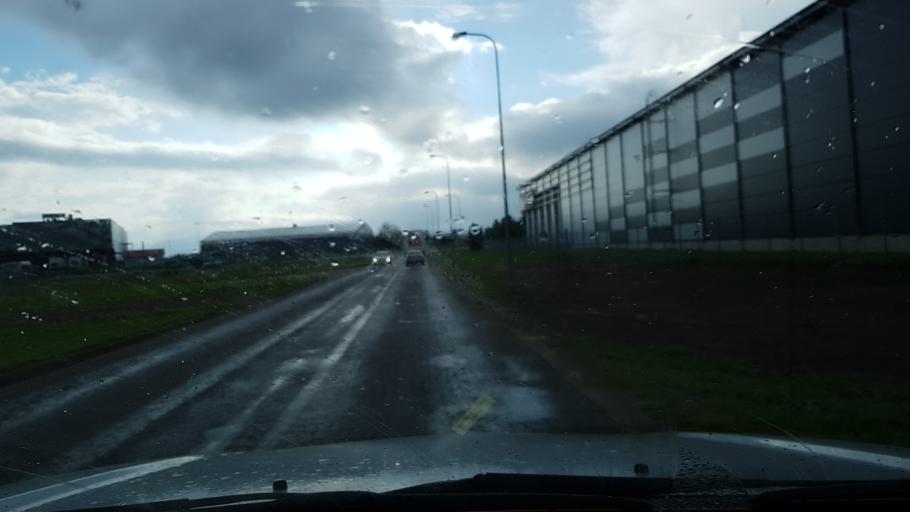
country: EE
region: Harju
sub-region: Rae vald
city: Jueri
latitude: 59.3613
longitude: 24.8856
